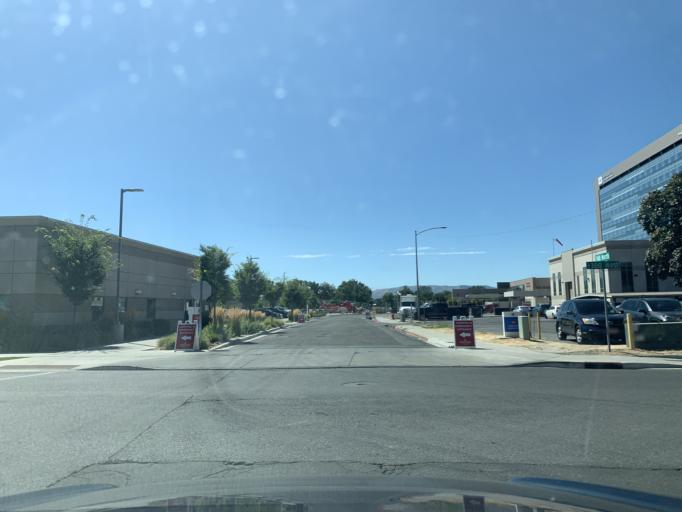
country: US
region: Utah
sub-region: Utah County
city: Provo
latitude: 40.2464
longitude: -111.6640
